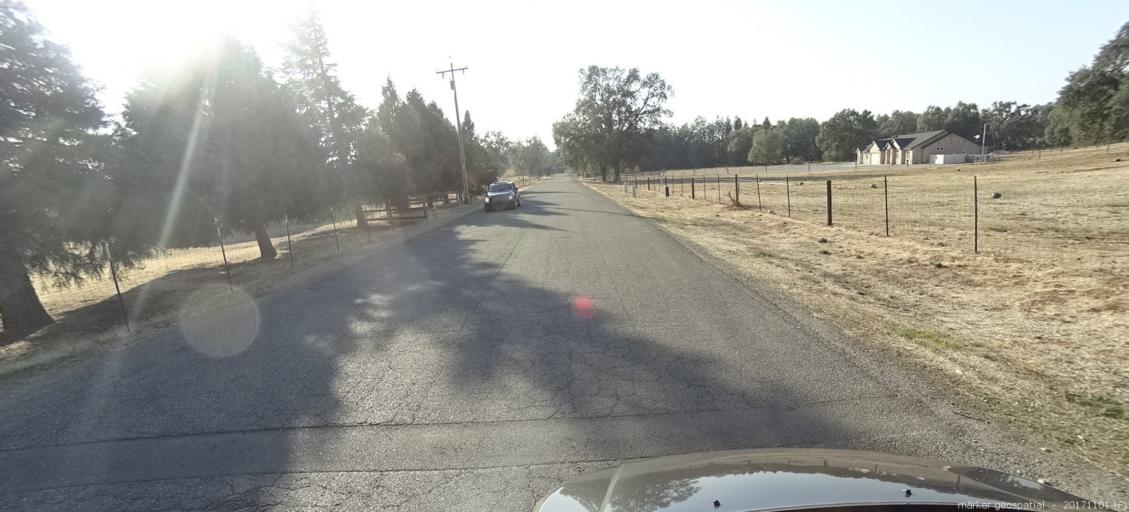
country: US
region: California
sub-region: Shasta County
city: Bella Vista
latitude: 40.6204
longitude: -122.3111
